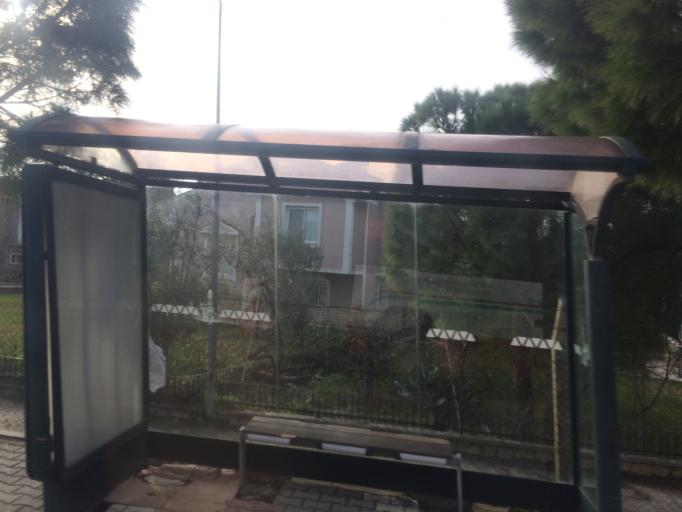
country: TR
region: Izmir
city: Menemen
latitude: 38.5056
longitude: 26.9585
